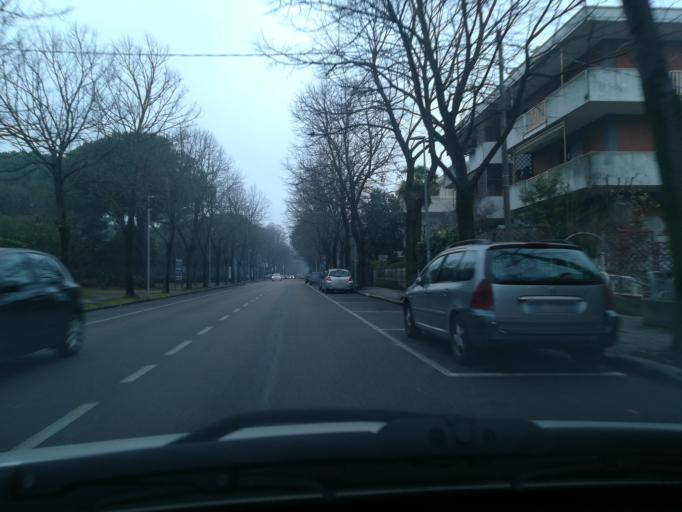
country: IT
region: Emilia-Romagna
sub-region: Provincia di Rimini
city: Riccione
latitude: 44.0063
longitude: 12.6461
